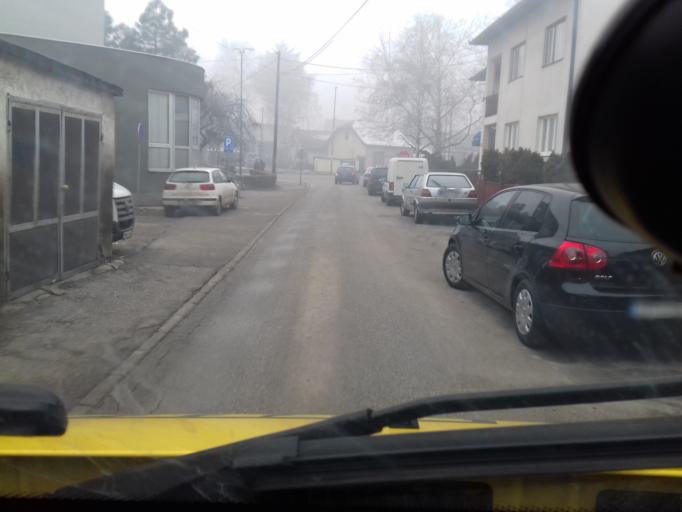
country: BA
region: Federation of Bosnia and Herzegovina
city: Visoko
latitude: 43.9917
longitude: 18.1812
